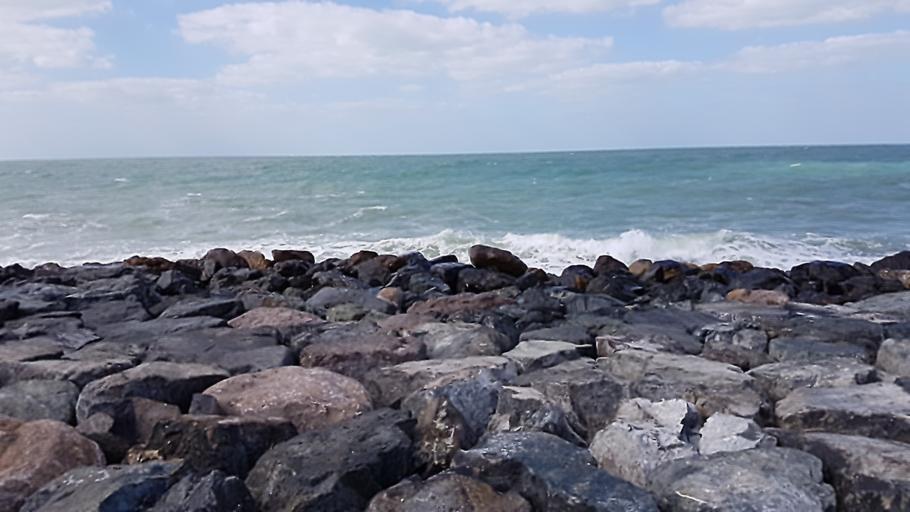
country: AE
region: Dubai
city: Dubai
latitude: 25.1327
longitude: 55.1170
